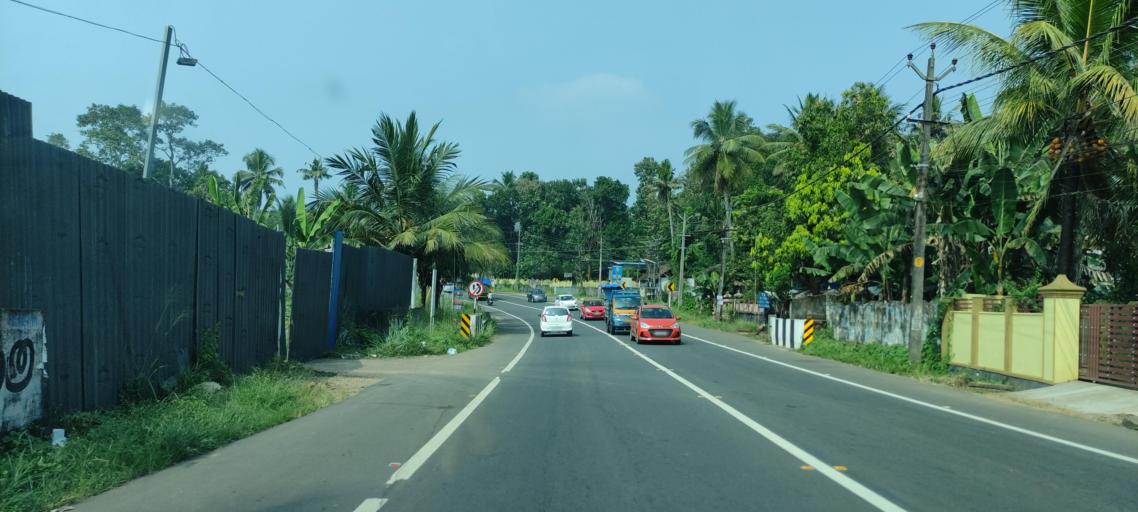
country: IN
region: Kerala
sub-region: Pattanamtitta
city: Adur
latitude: 9.2361
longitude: 76.6722
